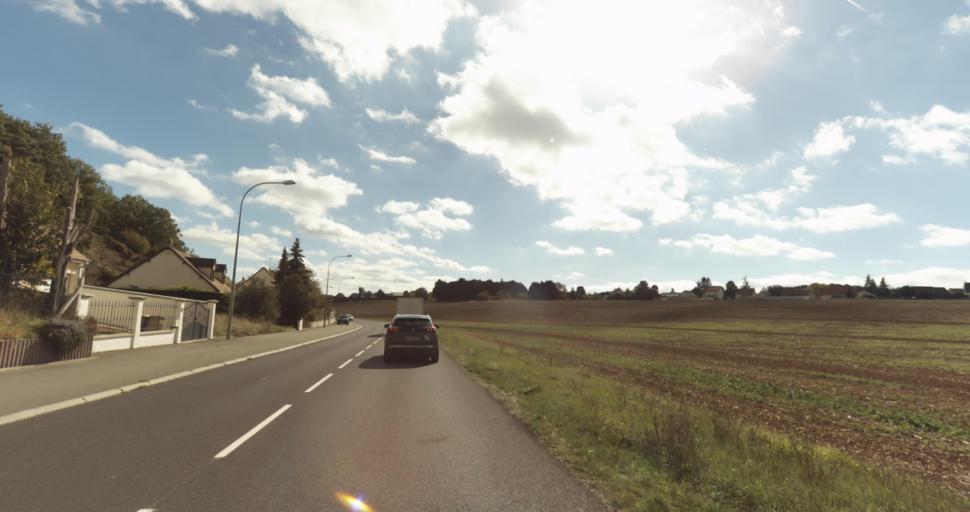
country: FR
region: Centre
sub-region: Departement d'Eure-et-Loir
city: Garnay
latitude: 48.7206
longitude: 1.3324
